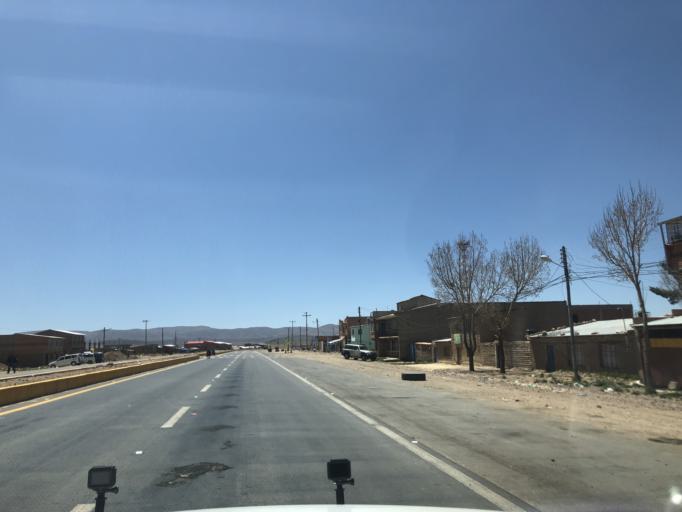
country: BO
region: La Paz
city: Colquiri
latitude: -17.6501
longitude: -67.2078
